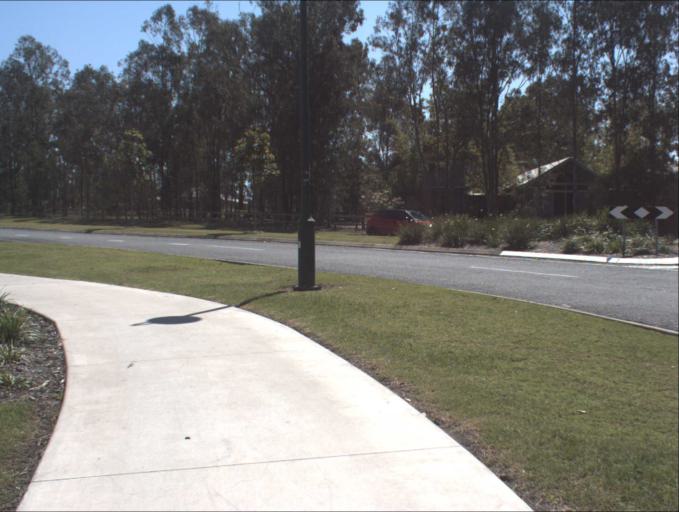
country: AU
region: Queensland
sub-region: Logan
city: North Maclean
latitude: -27.8120
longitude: 152.9604
